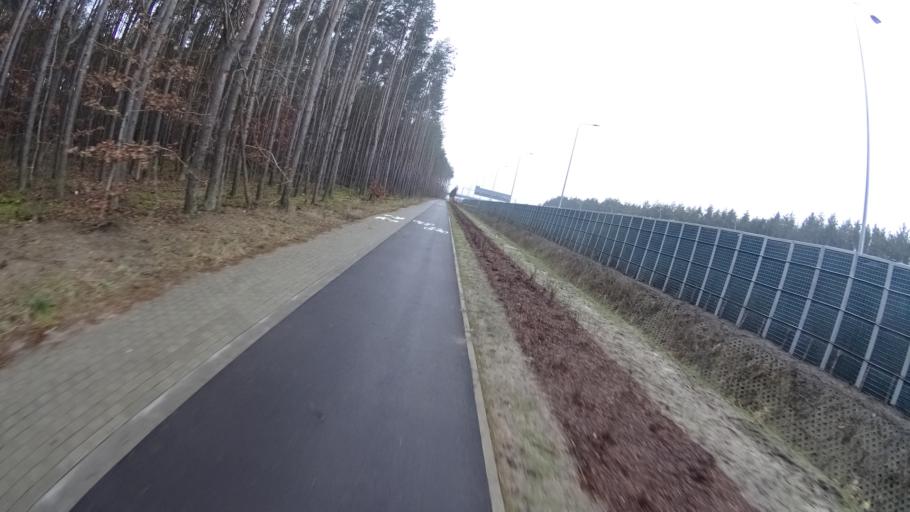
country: PL
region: Masovian Voivodeship
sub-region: Warszawa
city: Wawer
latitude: 52.1667
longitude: 21.1931
